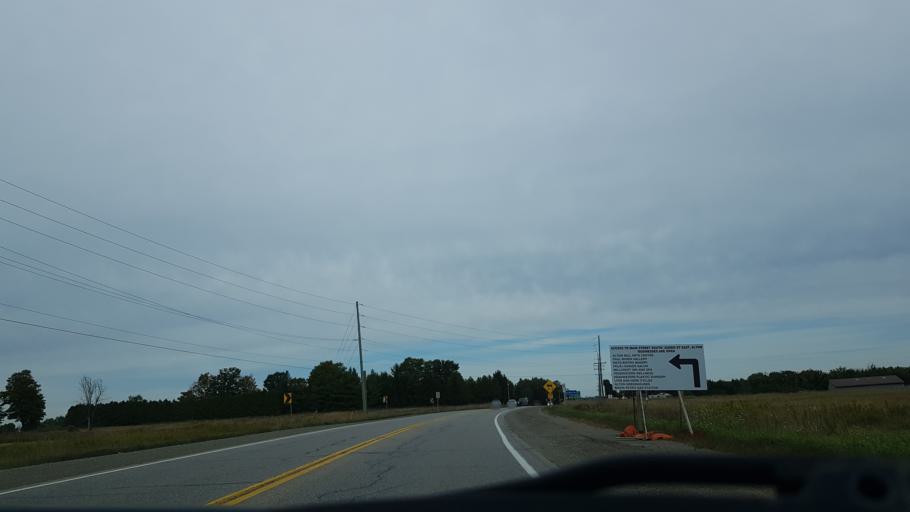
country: CA
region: Ontario
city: Orangeville
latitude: 43.8279
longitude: -80.0337
